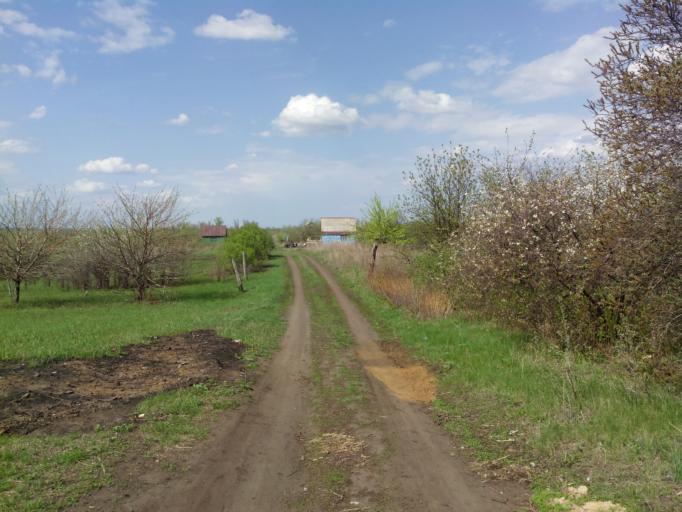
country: RU
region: Voronezj
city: Borisoglebsk
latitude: 51.3747
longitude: 42.1487
